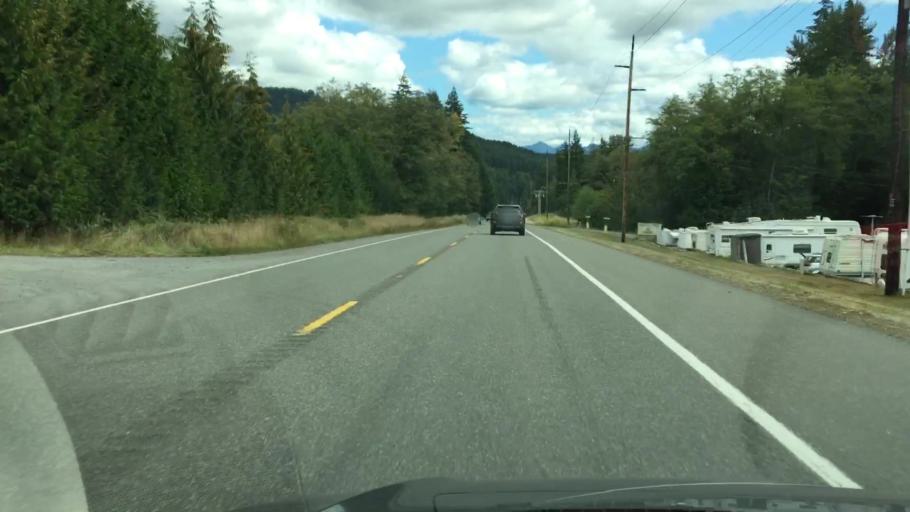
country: US
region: Washington
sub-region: Pierce County
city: Eatonville
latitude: 46.7837
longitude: -122.2470
